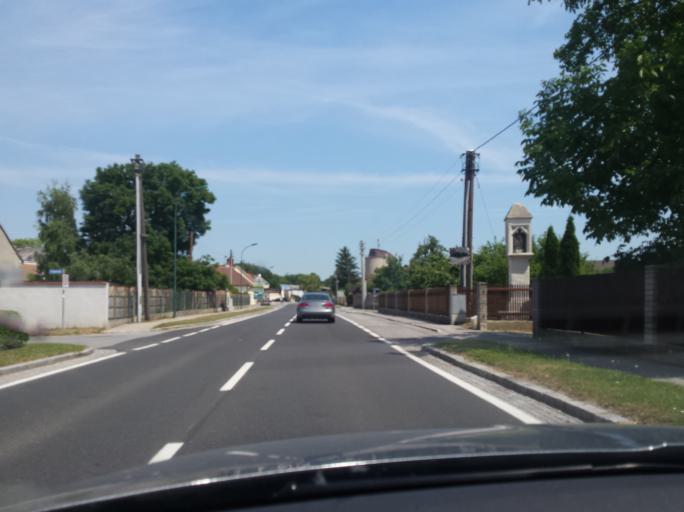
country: AT
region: Lower Austria
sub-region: Politischer Bezirk Bruck an der Leitha
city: Rohrau
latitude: 48.0569
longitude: 16.8443
